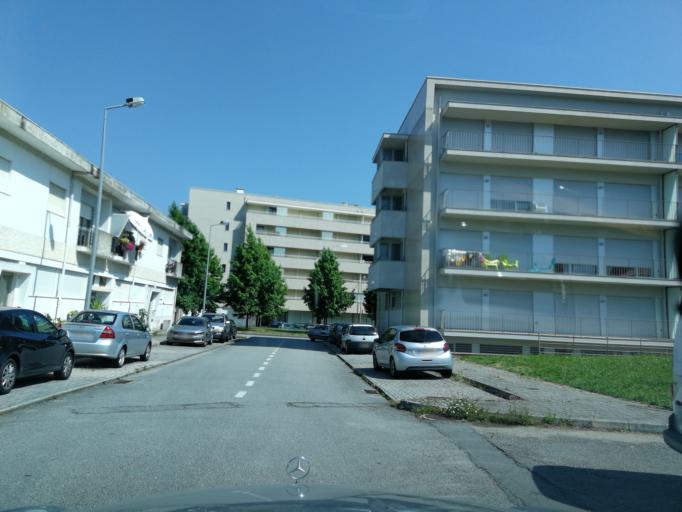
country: PT
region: Braga
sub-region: Braga
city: Adaufe
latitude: 41.5629
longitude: -8.3903
